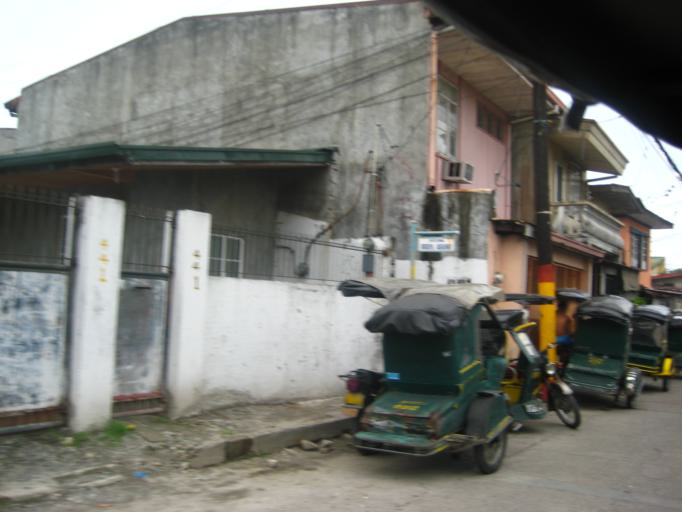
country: PH
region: Calabarzon
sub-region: Province of Rizal
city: Pateros
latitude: 14.5407
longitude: 121.0641
